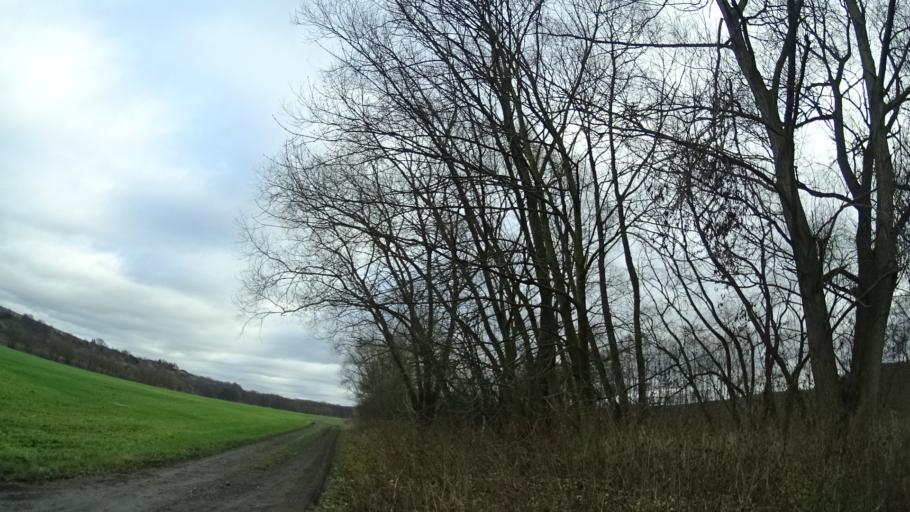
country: DE
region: Thuringia
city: Orlamunde
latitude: 50.7438
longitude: 11.4811
